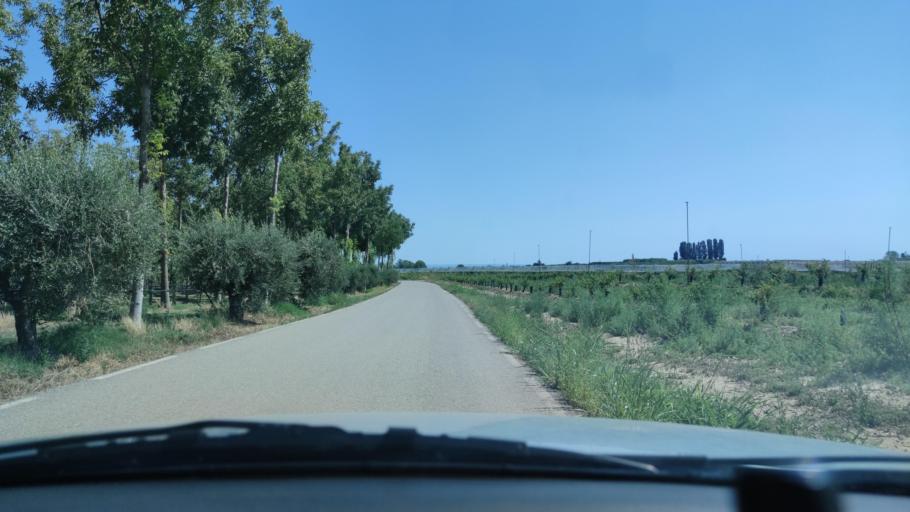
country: ES
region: Catalonia
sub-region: Provincia de Lleida
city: Torrefarrera
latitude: 41.6860
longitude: 0.6246
